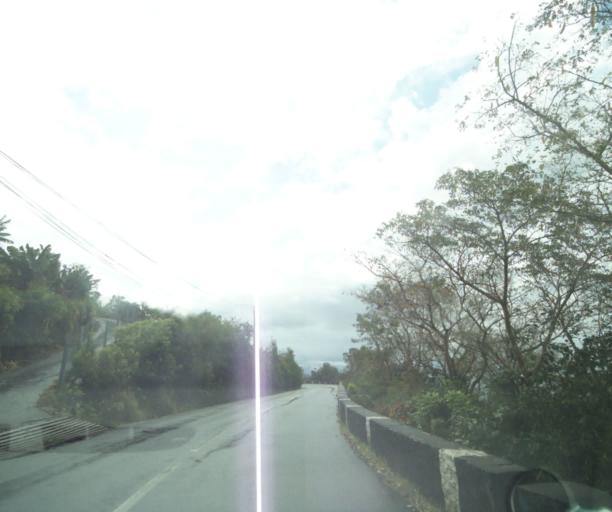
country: RE
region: Reunion
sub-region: Reunion
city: Saint-Paul
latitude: -21.0112
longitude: 55.3130
